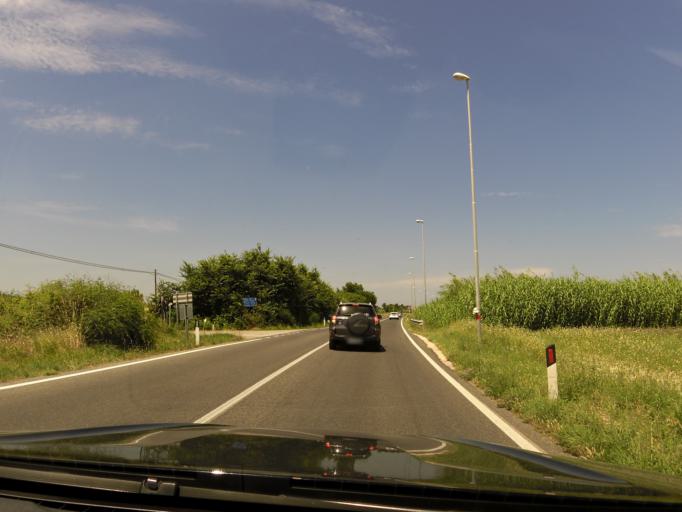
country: IT
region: The Marches
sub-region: Provincia di Pesaro e Urbino
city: Marotta
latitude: 43.7943
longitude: 13.0989
